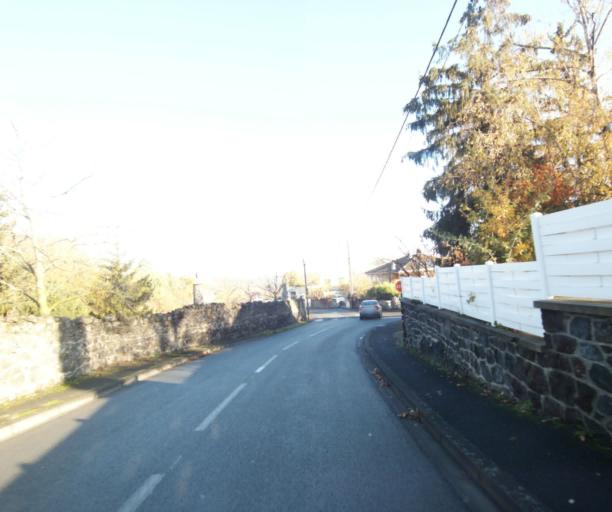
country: FR
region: Auvergne
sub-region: Departement du Puy-de-Dome
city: Nohanent
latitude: 45.8061
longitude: 3.0556
